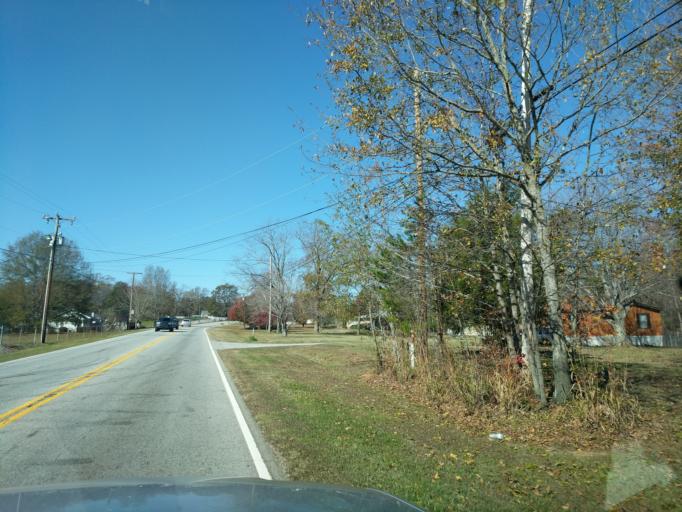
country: US
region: South Carolina
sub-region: Greenville County
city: Taylors
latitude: 34.9864
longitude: -82.3381
